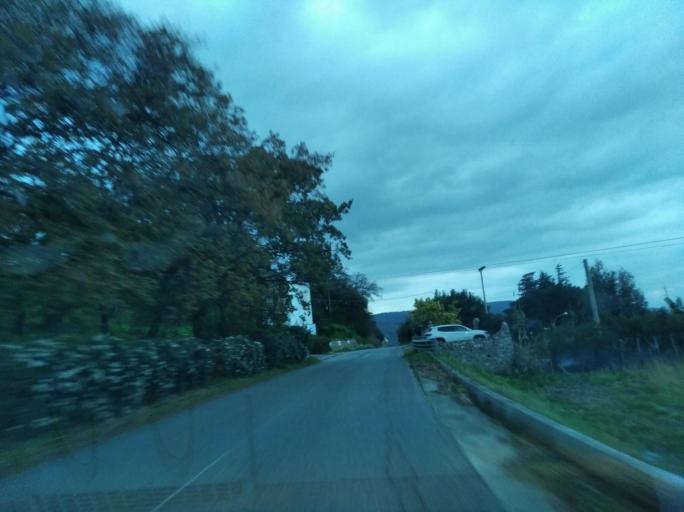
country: IT
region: Calabria
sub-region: Provincia di Catanzaro
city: Soverato Superiore
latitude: 38.7124
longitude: 16.5228
